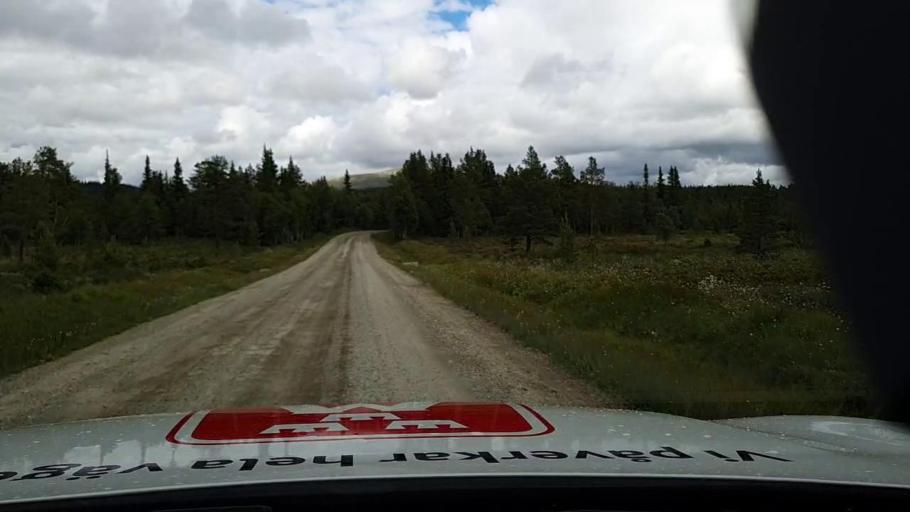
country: SE
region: Jaemtland
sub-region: Are Kommun
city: Jarpen
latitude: 62.5996
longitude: 13.2574
